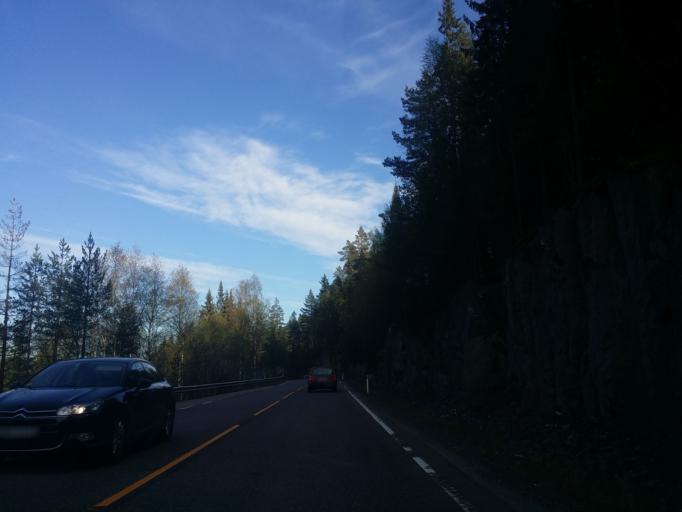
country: NO
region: Buskerud
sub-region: Kongsberg
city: Kongsberg
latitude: 59.6285
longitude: 9.5720
